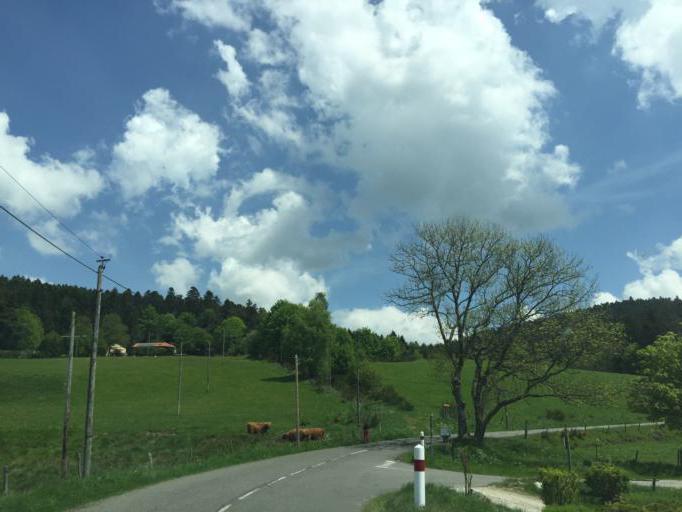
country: FR
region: Rhone-Alpes
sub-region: Departement de la Loire
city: Marlhes
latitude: 45.2837
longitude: 4.4465
